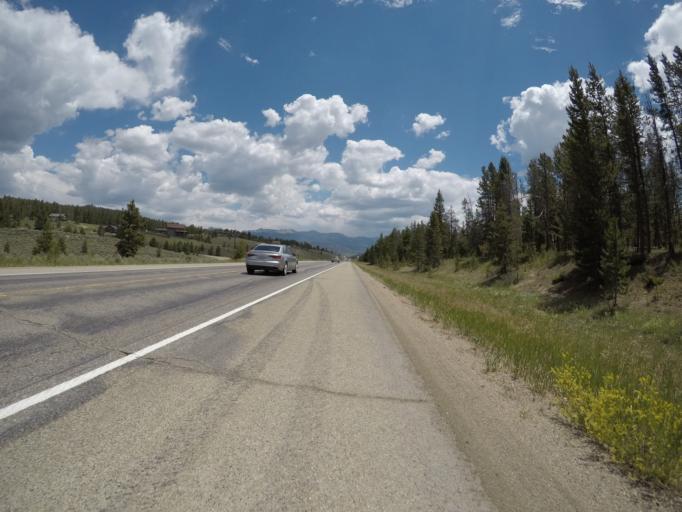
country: US
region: Colorado
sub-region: Grand County
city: Fraser
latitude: 39.9971
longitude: -105.8910
